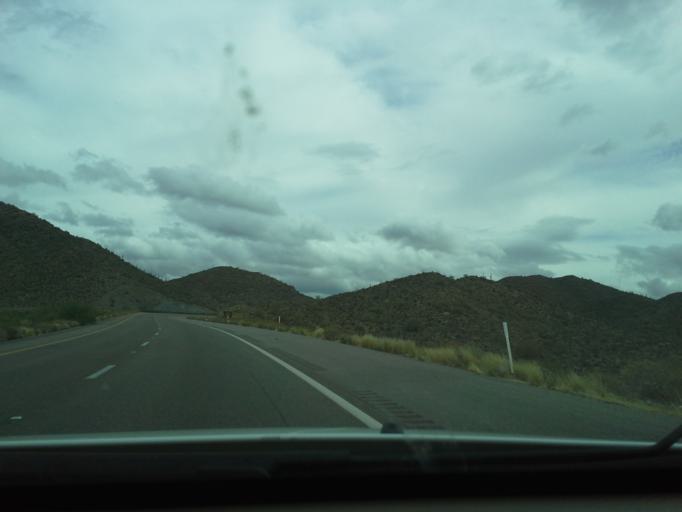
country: US
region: Arizona
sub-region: Pinal County
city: Gold Camp
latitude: 33.2668
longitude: -111.2487
